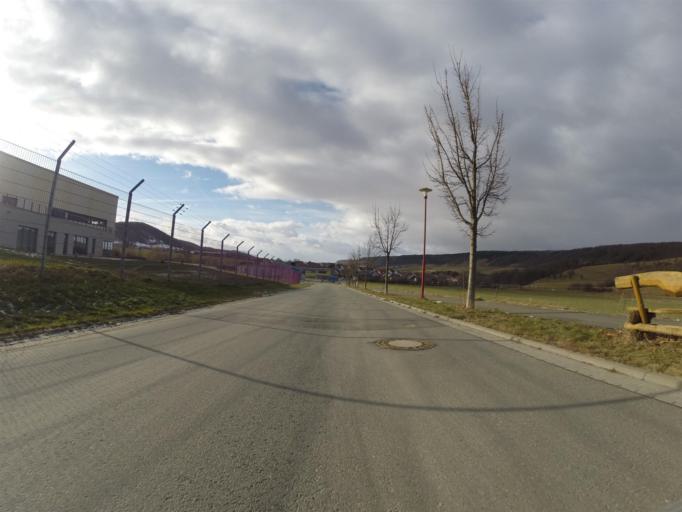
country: DE
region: Thuringia
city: Grosslobichau
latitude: 50.9265
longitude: 11.6886
